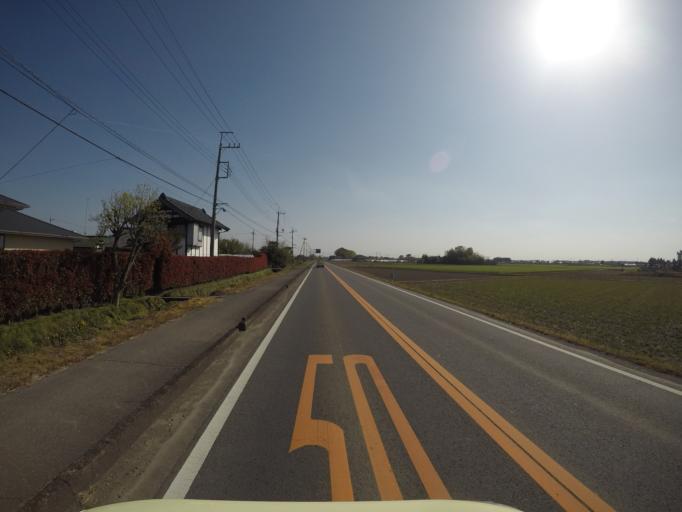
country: JP
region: Tochigi
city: Kaminokawa
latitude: 36.3691
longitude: 139.9079
